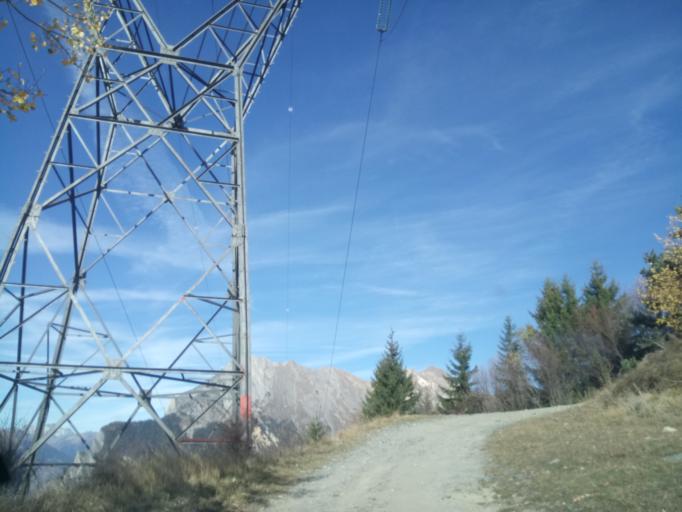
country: FR
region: Rhone-Alpes
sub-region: Departement de la Savoie
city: Saint-Michel-de-Maurienne
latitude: 45.2301
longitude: 6.4885
